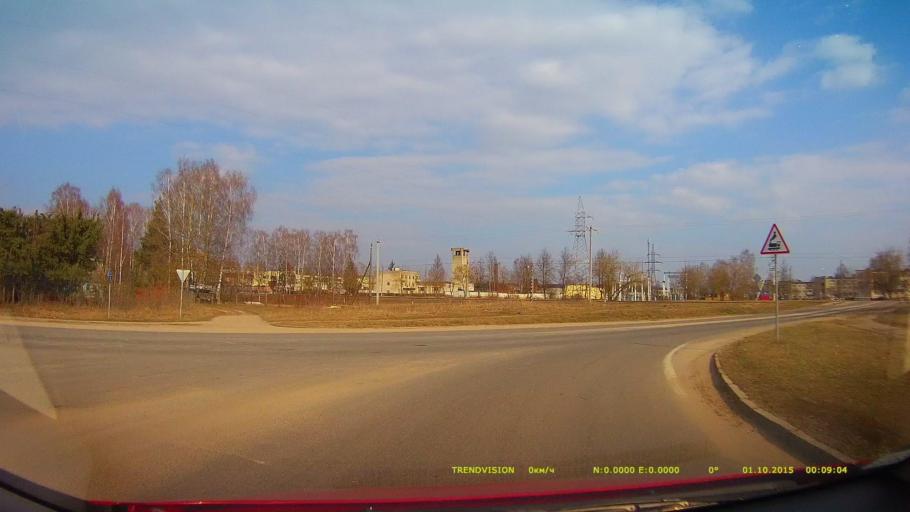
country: BY
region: Grodnenskaya
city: Lida
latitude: 53.9367
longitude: 25.2613
